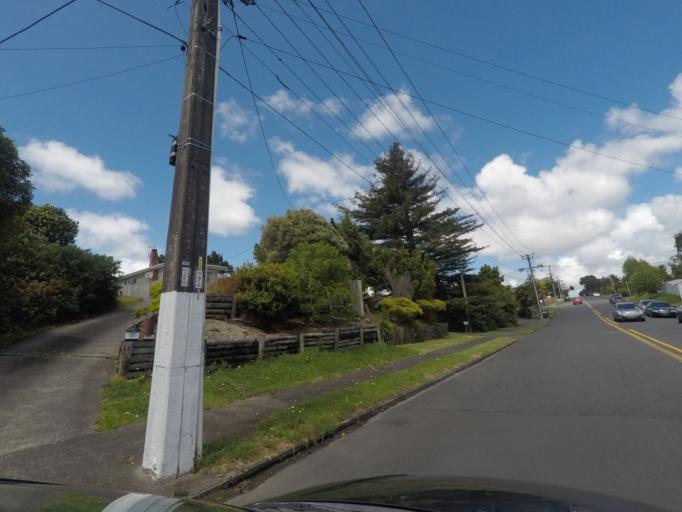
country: NZ
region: Auckland
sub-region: Auckland
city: Rosebank
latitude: -36.8767
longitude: 174.6433
